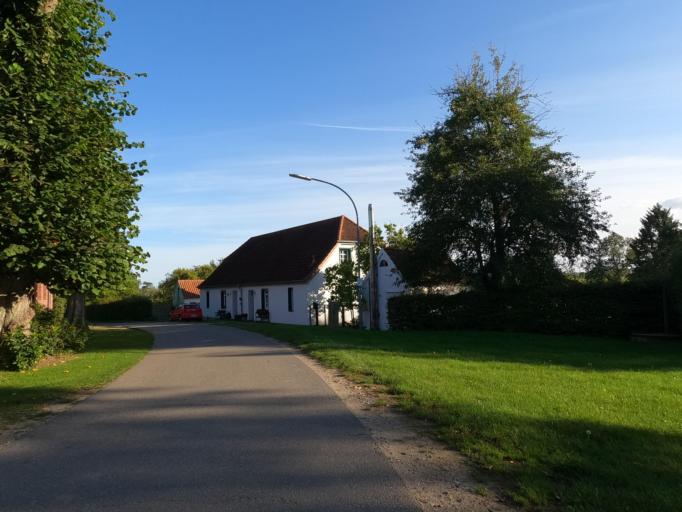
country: DE
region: Schleswig-Holstein
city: Neukirchen
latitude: 54.3136
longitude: 11.0240
